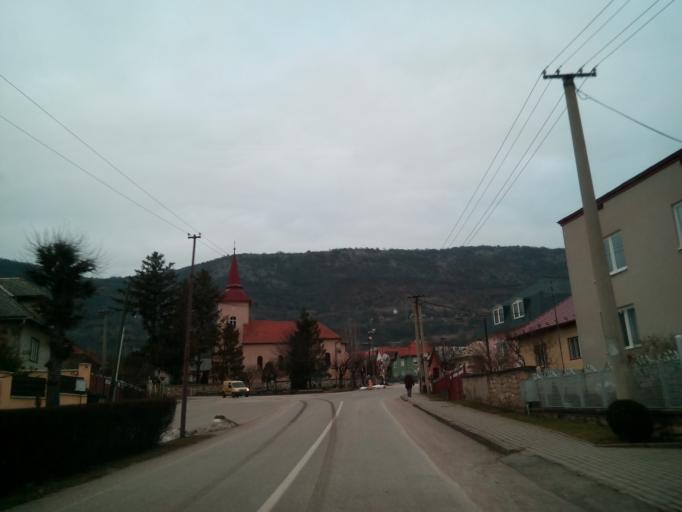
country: SK
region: Kosicky
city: Roznava
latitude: 48.5926
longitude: 20.6724
